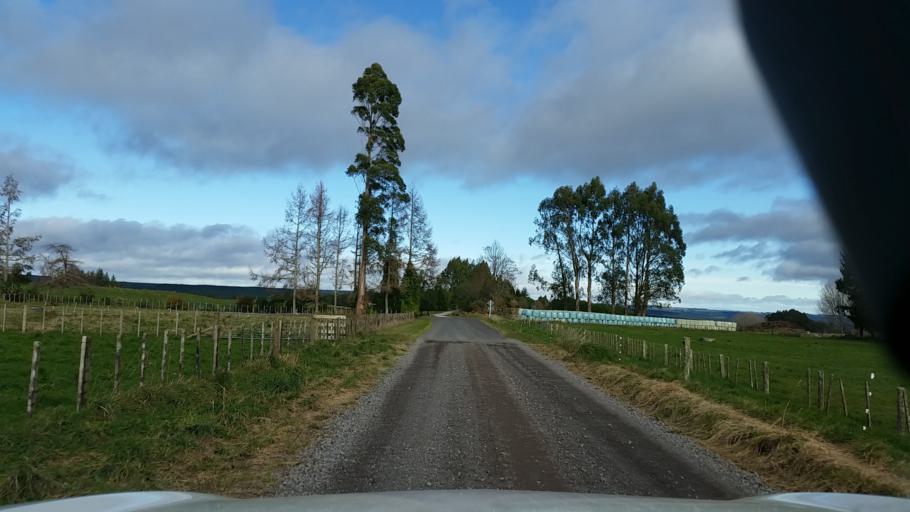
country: NZ
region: Bay of Plenty
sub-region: Whakatane District
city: Murupara
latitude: -38.4787
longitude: 176.4147
